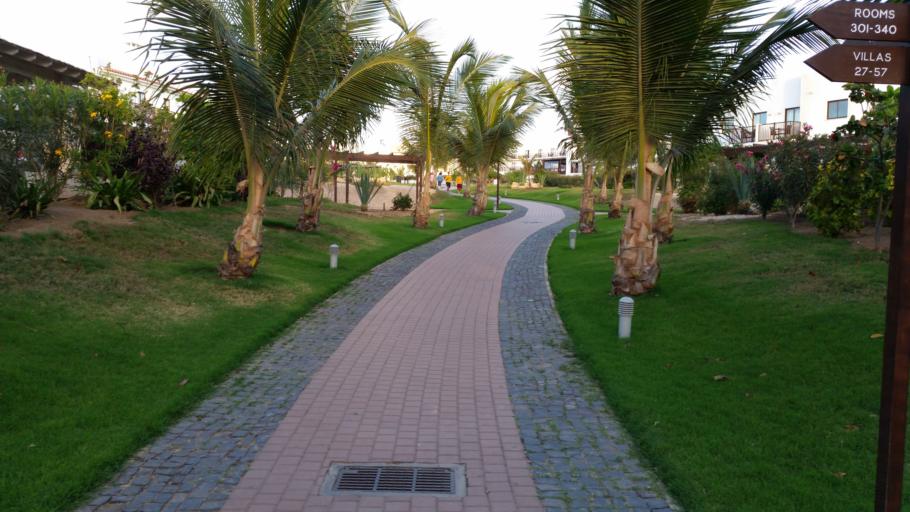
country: CV
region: Sal
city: Santa Maria
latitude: 16.6162
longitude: -22.9257
